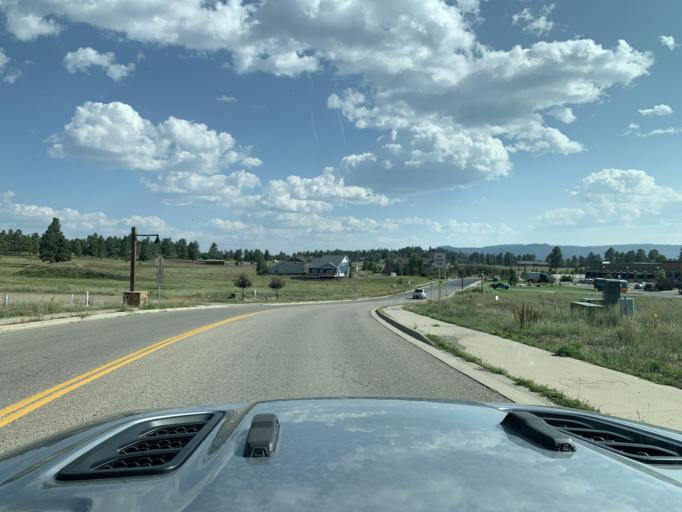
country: US
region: Colorado
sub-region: Archuleta County
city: Pagosa Springs
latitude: 37.2618
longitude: -107.0609
